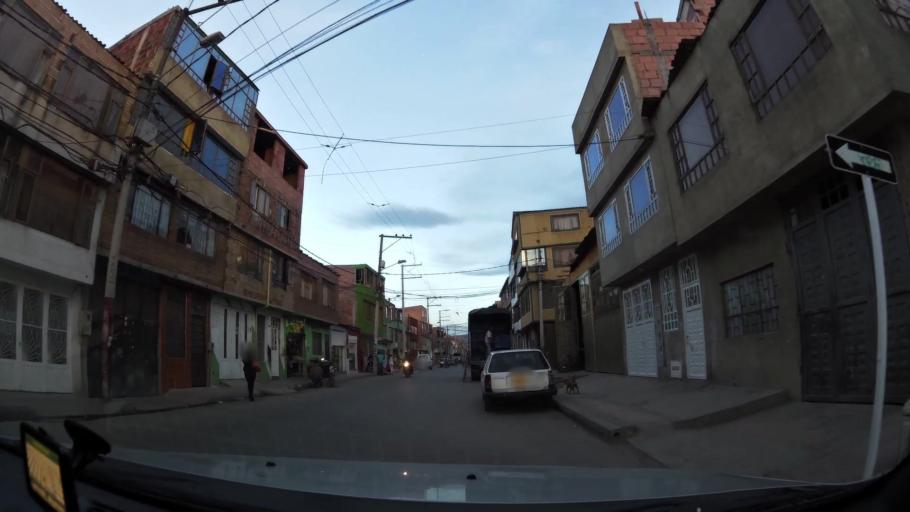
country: CO
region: Cundinamarca
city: Soacha
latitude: 4.6271
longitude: -74.1645
